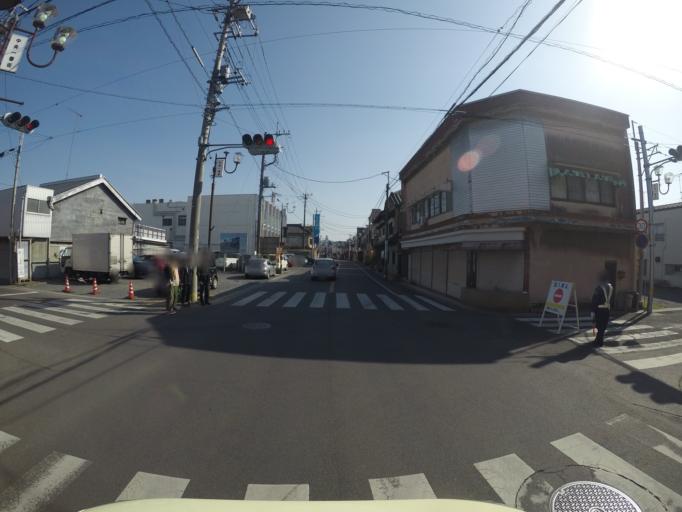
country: JP
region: Ibaraki
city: Yuki
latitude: 36.3033
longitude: 139.8745
